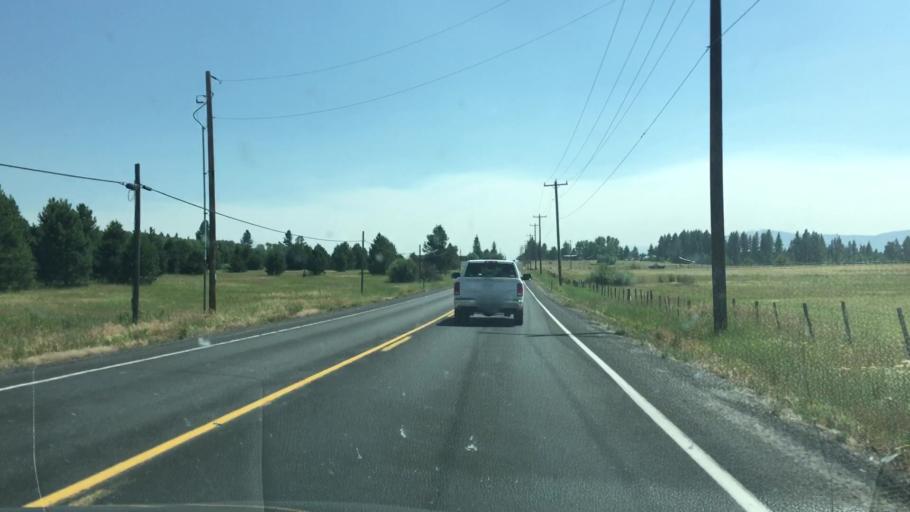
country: US
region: Idaho
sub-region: Valley County
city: McCall
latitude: 44.8790
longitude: -116.0907
